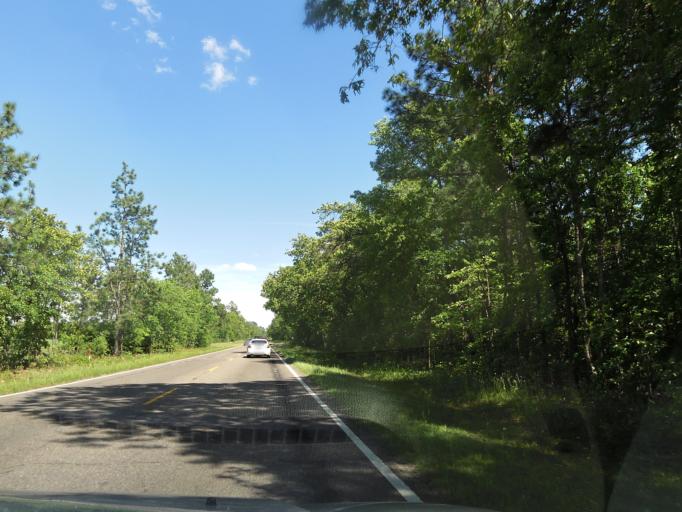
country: US
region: South Carolina
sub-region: Barnwell County
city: Williston
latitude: 33.5059
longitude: -81.5458
